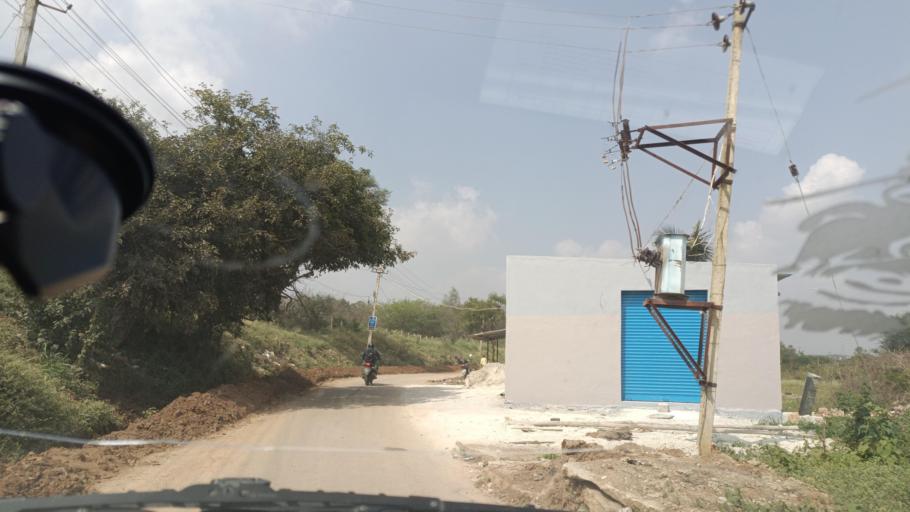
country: IN
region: Karnataka
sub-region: Bangalore Urban
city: Yelahanka
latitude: 13.1743
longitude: 77.6323
